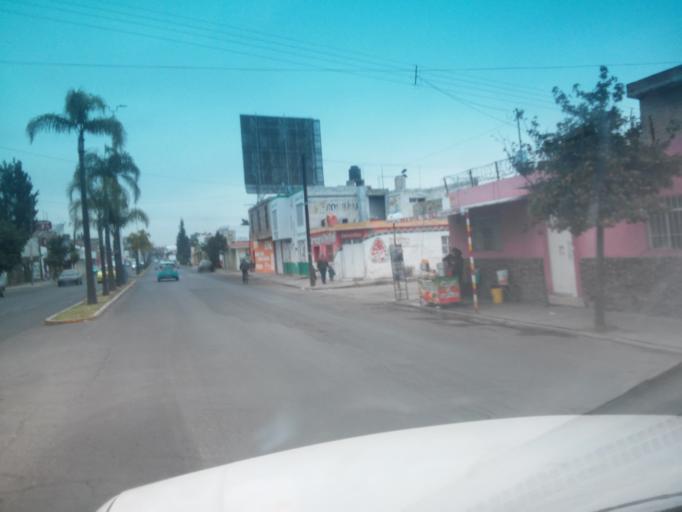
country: MX
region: Durango
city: Victoria de Durango
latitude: 24.0095
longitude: -104.6789
